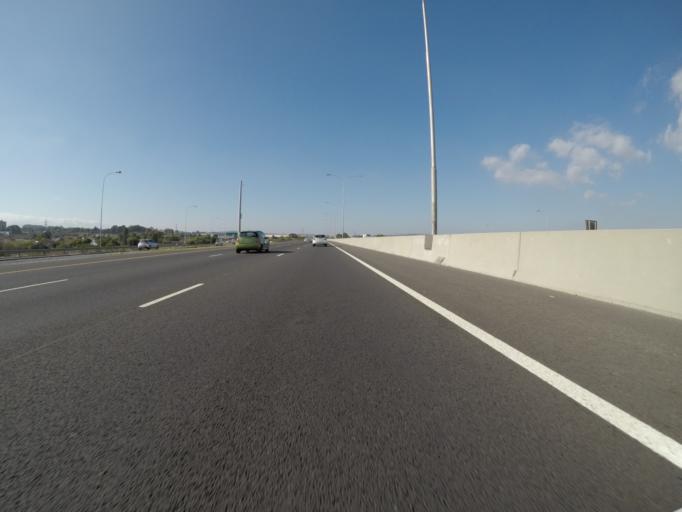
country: ZA
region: Western Cape
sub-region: City of Cape Town
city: Kraaifontein
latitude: -33.9169
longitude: 18.6671
